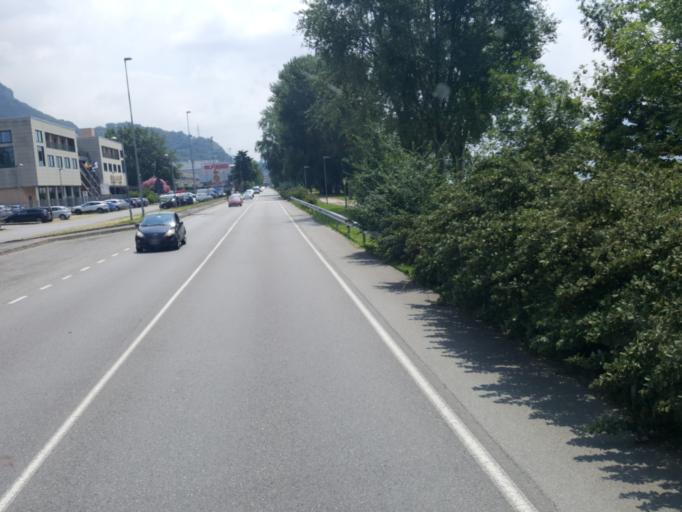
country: IT
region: Lombardy
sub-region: Provincia di Lecco
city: Pescate
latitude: 45.8290
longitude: 9.4097
